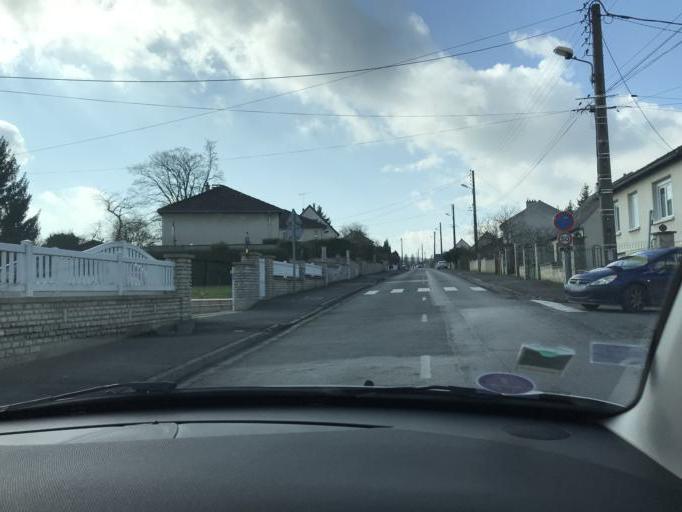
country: FR
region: Picardie
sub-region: Departement de l'Aisne
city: Billy-sur-Aisne
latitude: 49.3602
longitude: 3.3876
